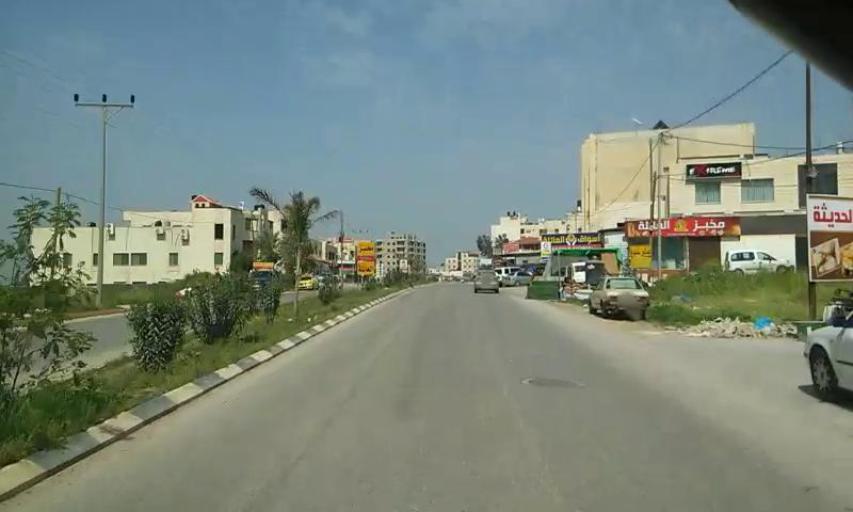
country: PS
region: West Bank
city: Janin
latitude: 32.4841
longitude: 35.2996
